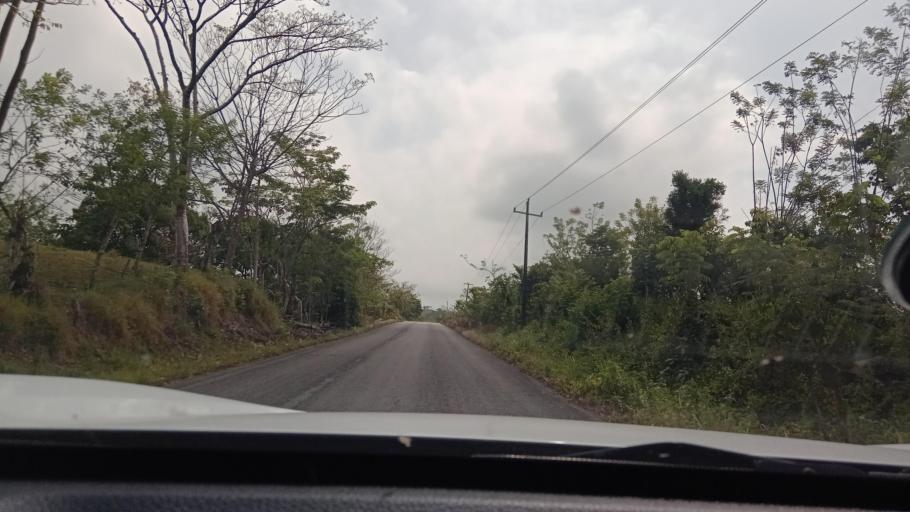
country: MX
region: Tabasco
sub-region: Huimanguillo
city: Francisco Rueda
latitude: 17.5742
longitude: -94.1062
